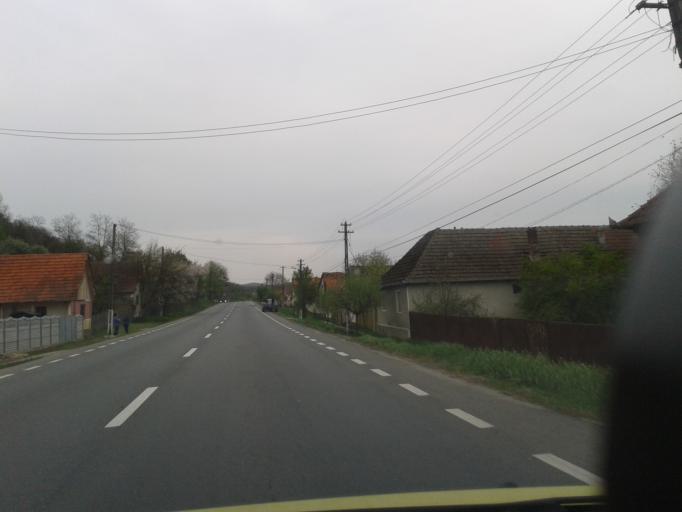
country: RO
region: Arad
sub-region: Comuna Ususau
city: Ususau
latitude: 46.1117
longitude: 21.8312
